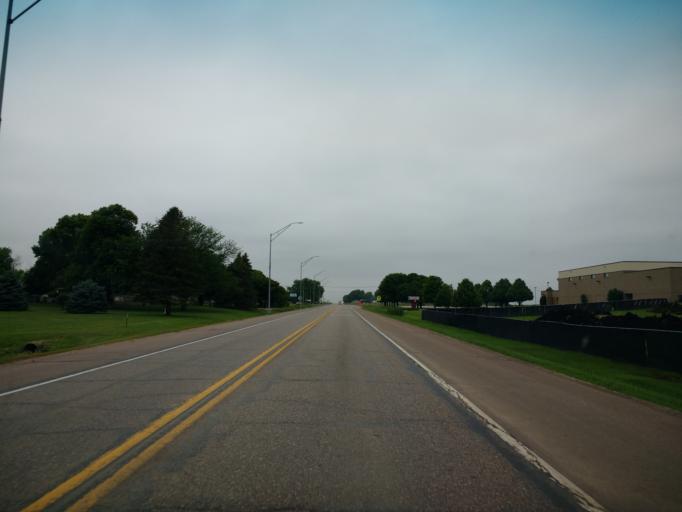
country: US
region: Iowa
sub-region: O'Brien County
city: Hartley
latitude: 43.1849
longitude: -95.4831
